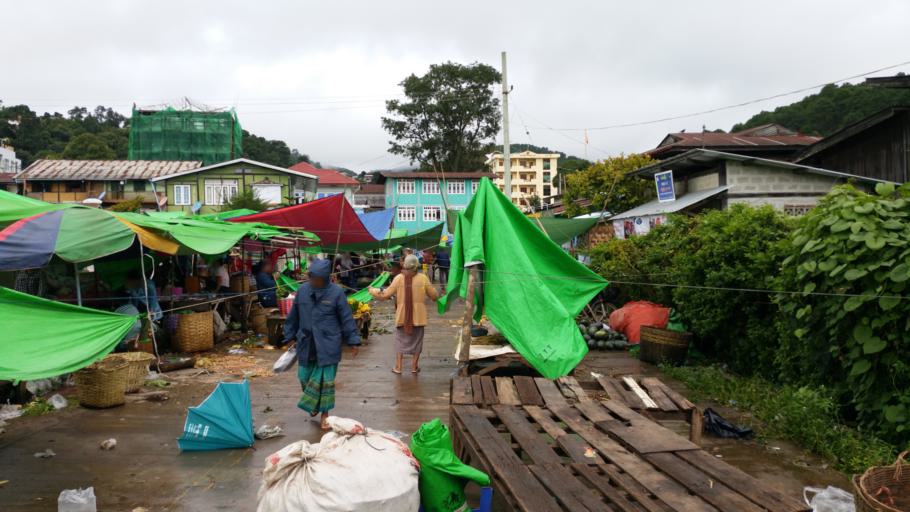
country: MM
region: Mandalay
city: Yamethin
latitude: 20.6348
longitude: 96.5681
